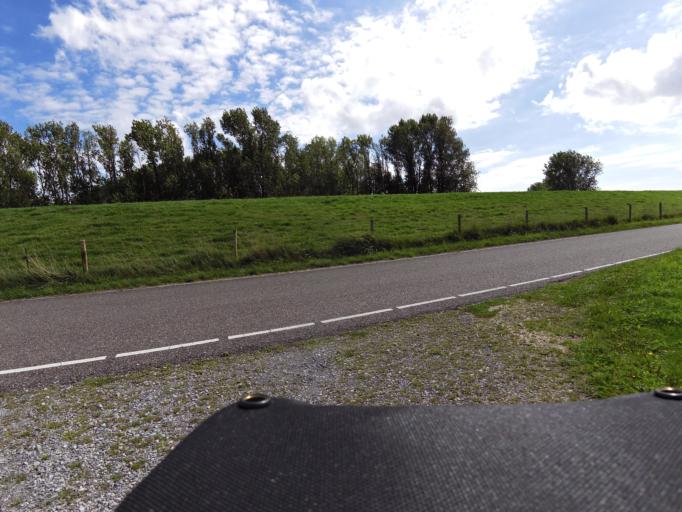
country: NL
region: South Holland
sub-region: Gemeente Goeree-Overflakkee
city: Goedereede
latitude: 51.7767
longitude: 4.0354
